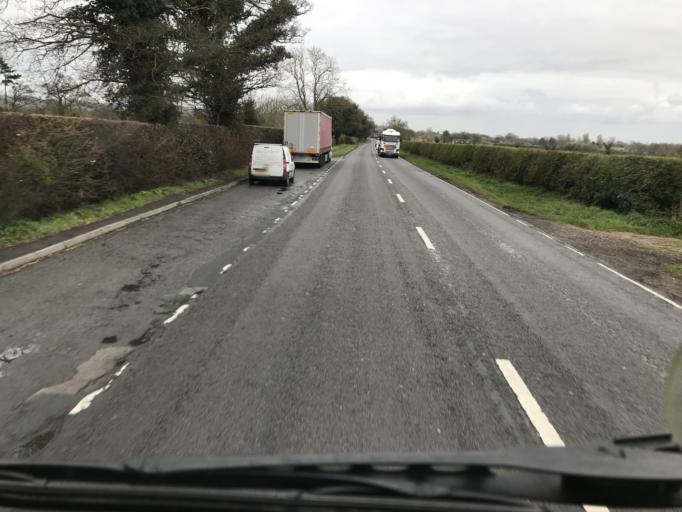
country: GB
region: England
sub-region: Cheshire West and Chester
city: Waverton
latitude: 53.1340
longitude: -2.8078
